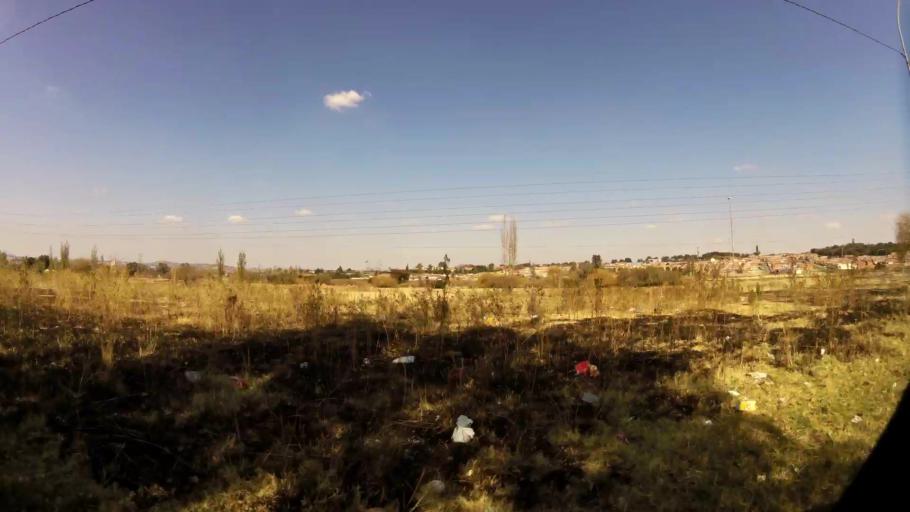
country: ZA
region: Gauteng
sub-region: City of Johannesburg Metropolitan Municipality
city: Soweto
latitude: -26.2375
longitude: 27.8729
